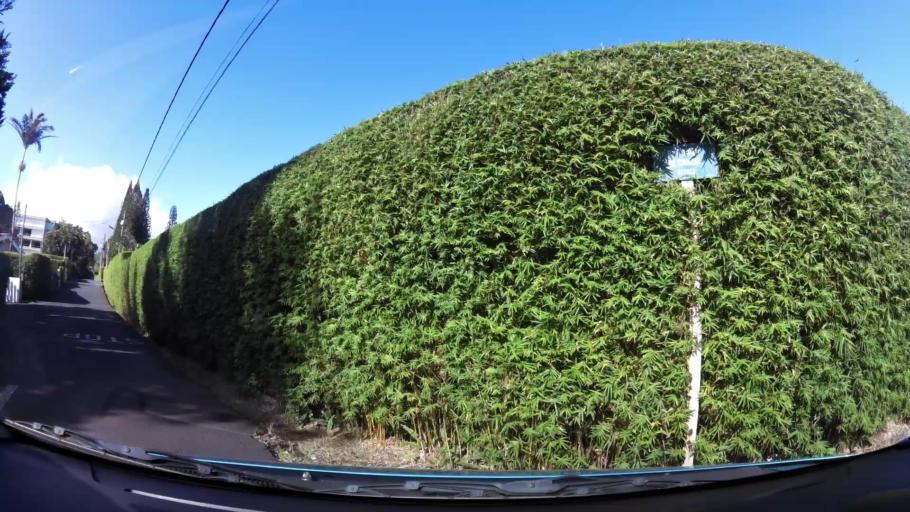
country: MU
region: Plaines Wilhems
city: Curepipe
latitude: -20.3091
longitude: 57.5018
